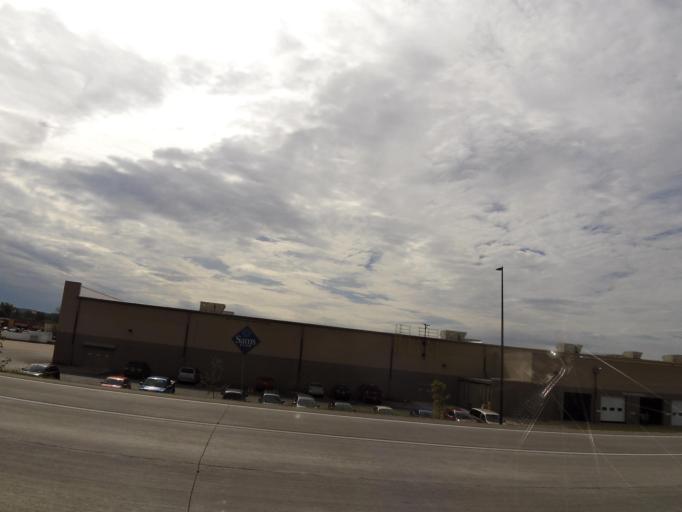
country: US
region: Wisconsin
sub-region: La Crosse County
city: Onalaska
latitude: 43.8717
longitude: -91.2153
